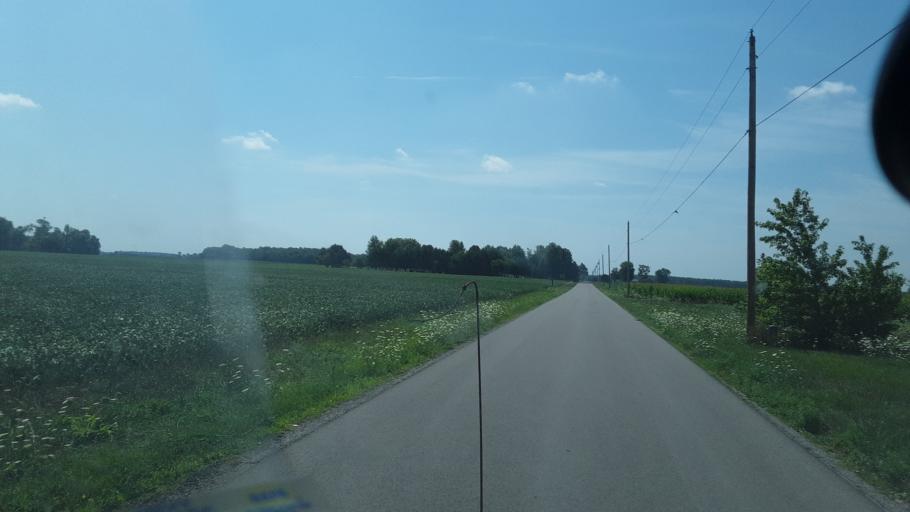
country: US
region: Ohio
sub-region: Hancock County
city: Findlay
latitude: 41.0045
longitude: -83.5160
